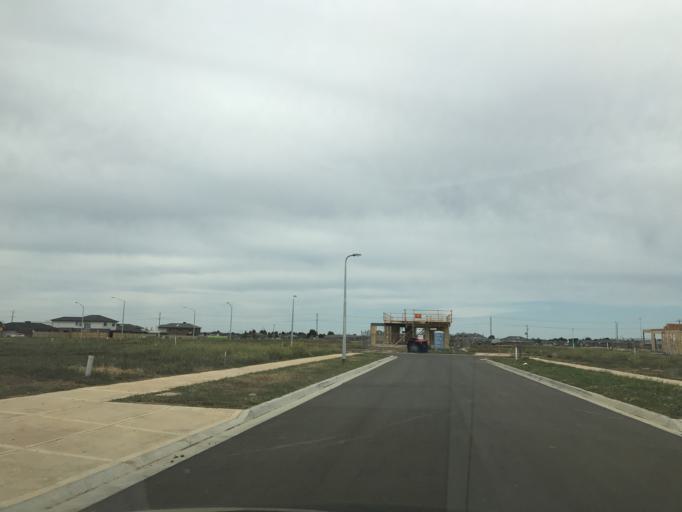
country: AU
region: Victoria
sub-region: Wyndham
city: Truganina
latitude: -37.8341
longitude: 144.7218
